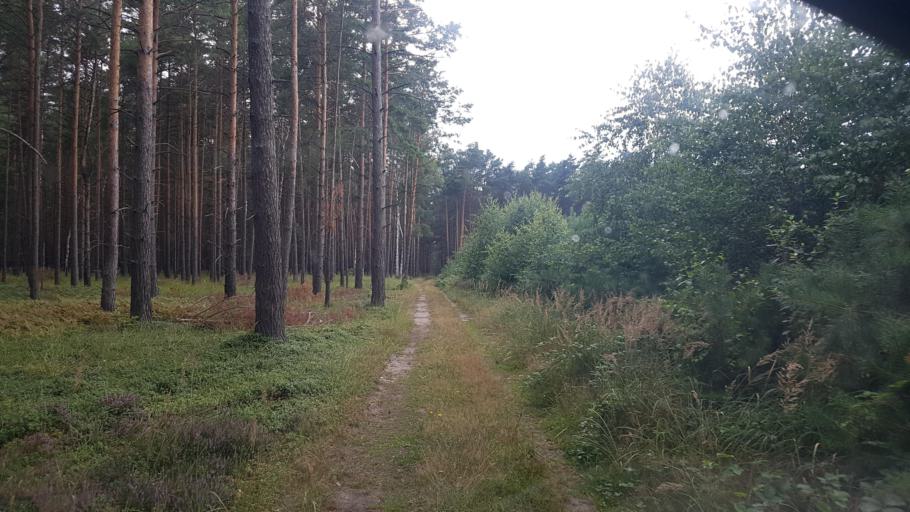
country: DE
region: Brandenburg
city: Sallgast
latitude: 51.5830
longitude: 13.9055
